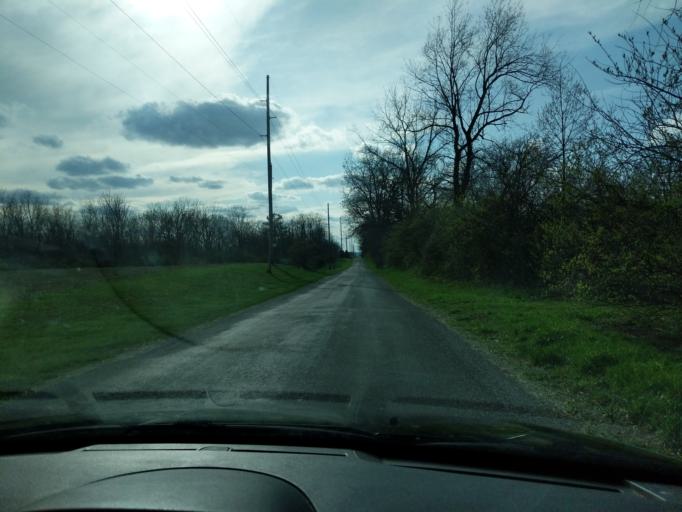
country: US
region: Ohio
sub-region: Champaign County
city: North Lewisburg
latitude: 40.1631
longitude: -83.6469
